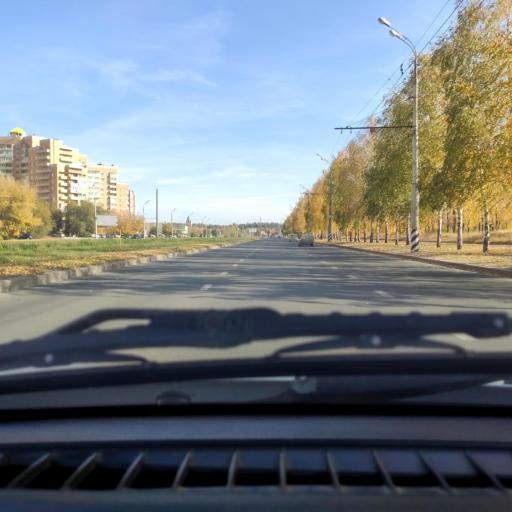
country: RU
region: Samara
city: Tol'yatti
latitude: 53.4986
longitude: 49.2794
